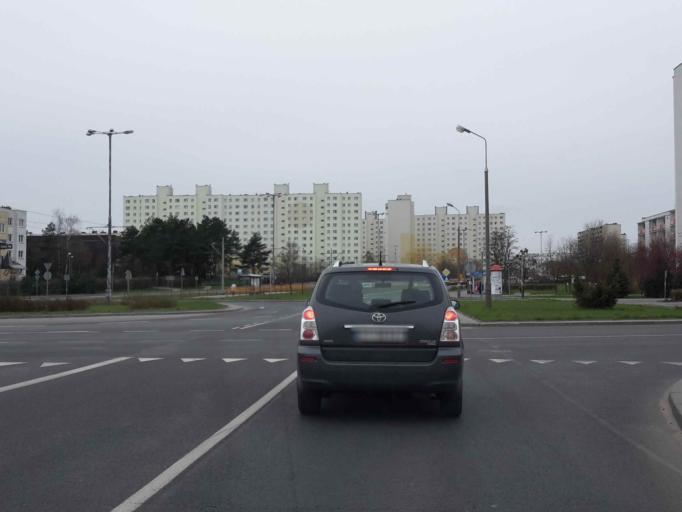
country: PL
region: Kujawsko-Pomorskie
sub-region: Powiat torunski
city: Lubicz Dolny
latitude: 53.0230
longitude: 18.6898
